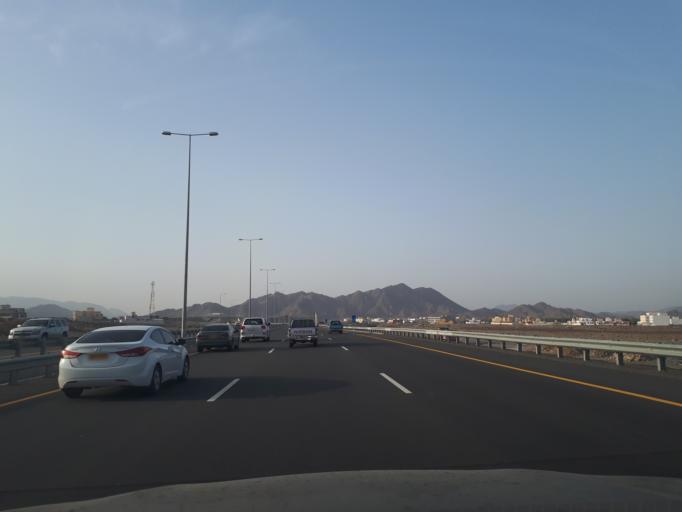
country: OM
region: Muhafazat ad Dakhiliyah
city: Bidbid
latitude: 23.3210
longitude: 58.1155
